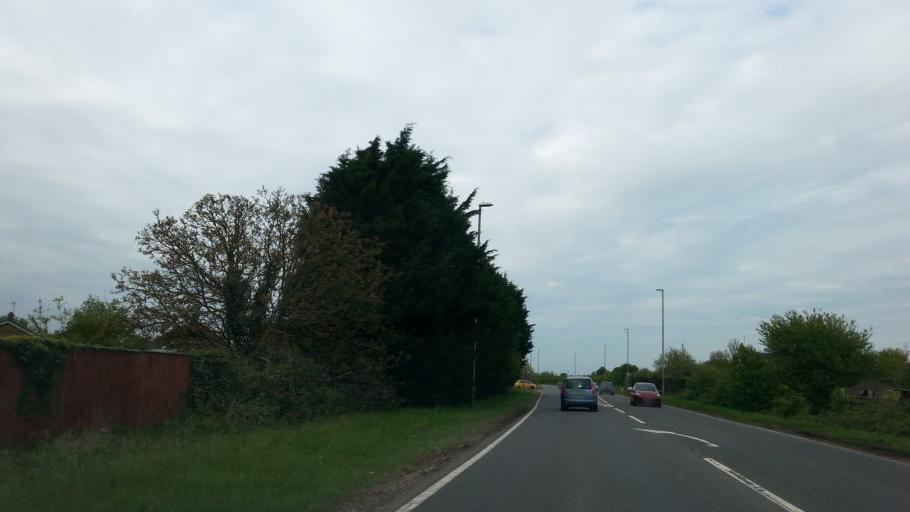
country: GB
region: England
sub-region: Cambridgeshire
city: Doddington
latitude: 52.5117
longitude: 0.0885
